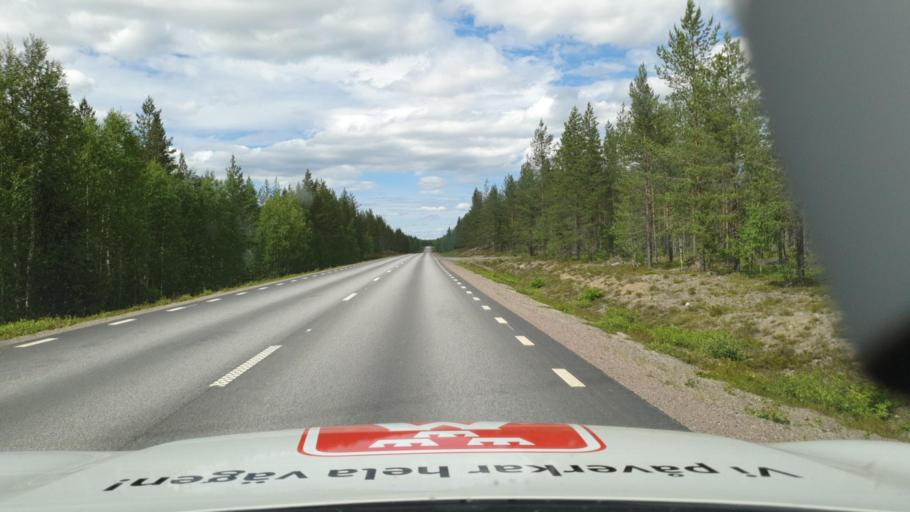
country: SE
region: Vaesterbotten
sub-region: Skelleftea Kommun
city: Langsele
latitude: 65.1325
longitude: 19.9187
